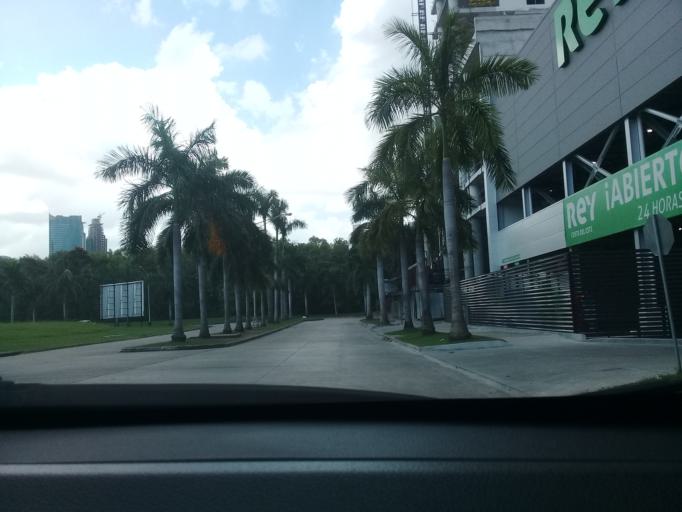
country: PA
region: Panama
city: San Miguelito
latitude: 9.0156
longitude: -79.4681
